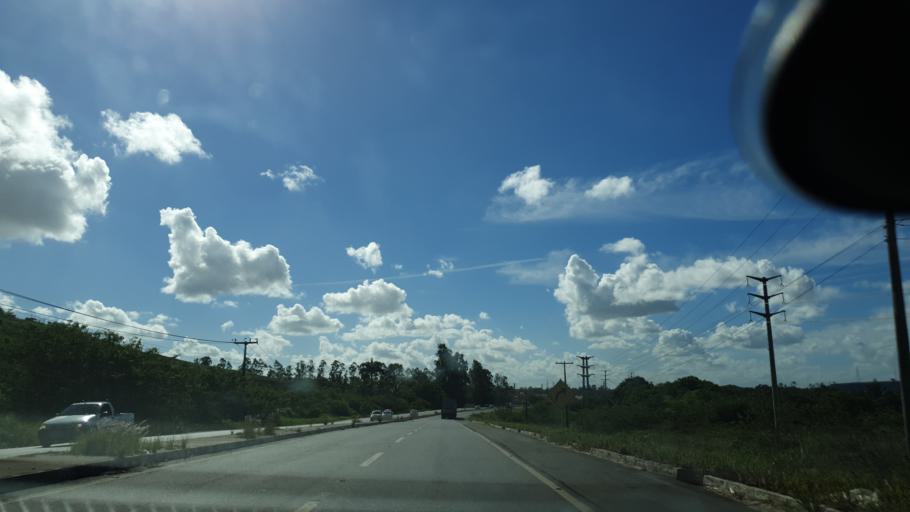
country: BR
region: Bahia
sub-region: Camacari
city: Camacari
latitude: -12.6851
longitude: -38.2588
